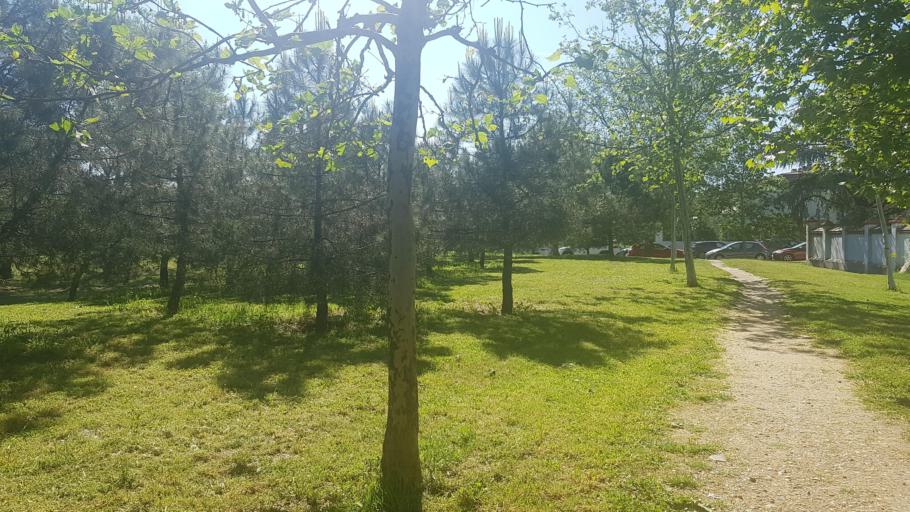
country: ES
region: Madrid
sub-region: Provincia de Madrid
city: Pozuelo de Alarcon
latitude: 40.4666
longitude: -3.7865
